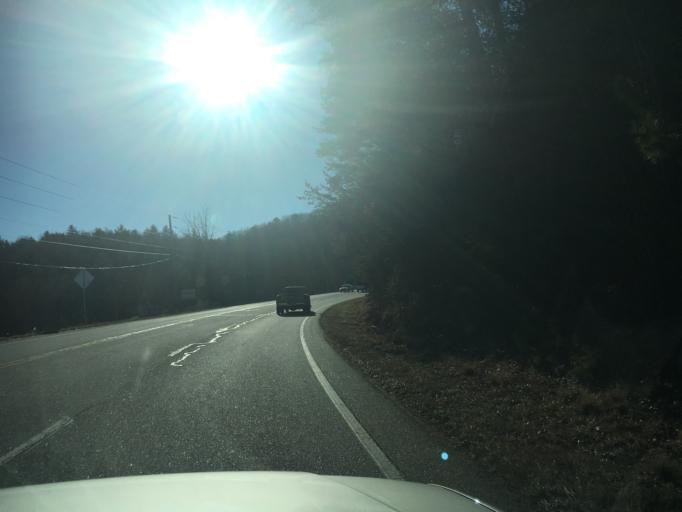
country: US
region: Georgia
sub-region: Union County
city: Blairsville
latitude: 34.7927
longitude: -83.8948
